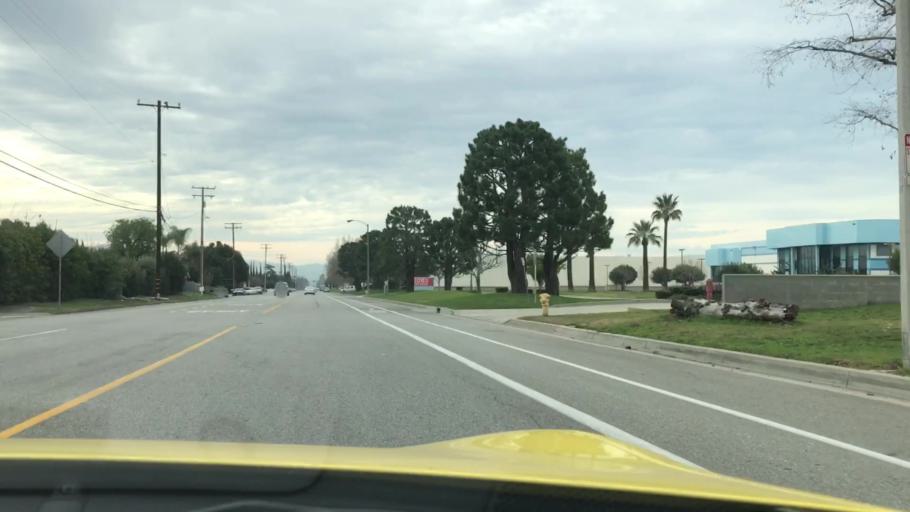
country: US
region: California
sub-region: San Bernardino County
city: Chino
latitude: 34.0100
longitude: -117.6980
